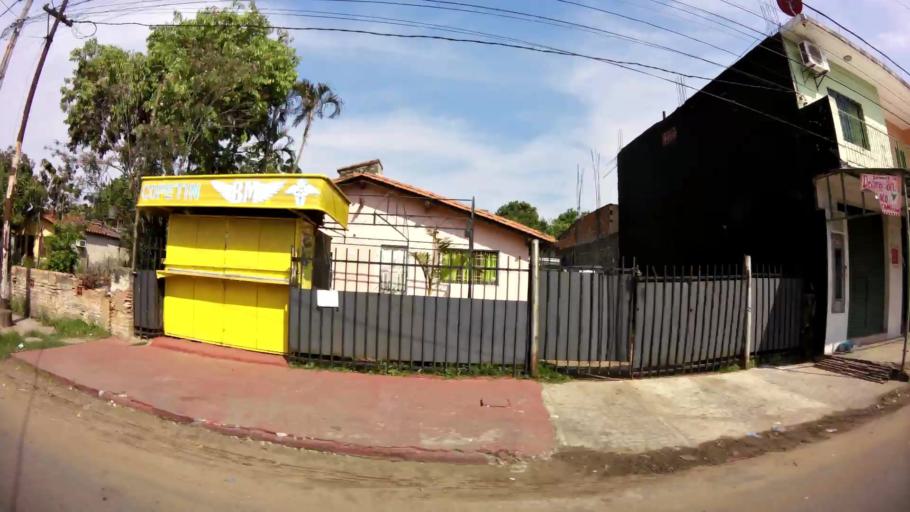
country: PY
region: Central
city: Fernando de la Mora
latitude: -25.2706
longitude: -57.5470
